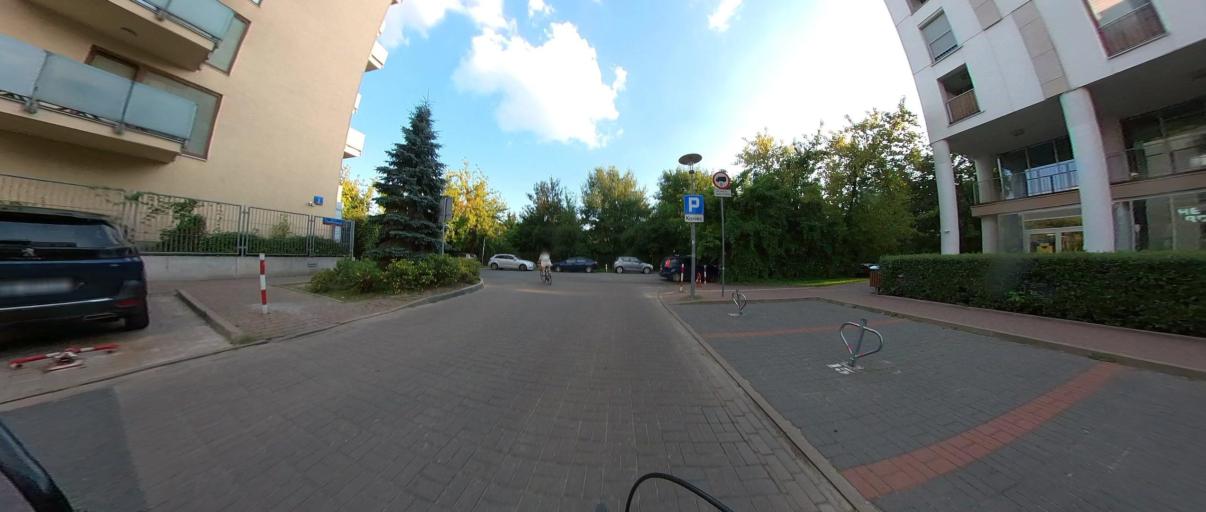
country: PL
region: Masovian Voivodeship
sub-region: Warszawa
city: Ochota
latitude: 52.2022
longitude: 20.9957
